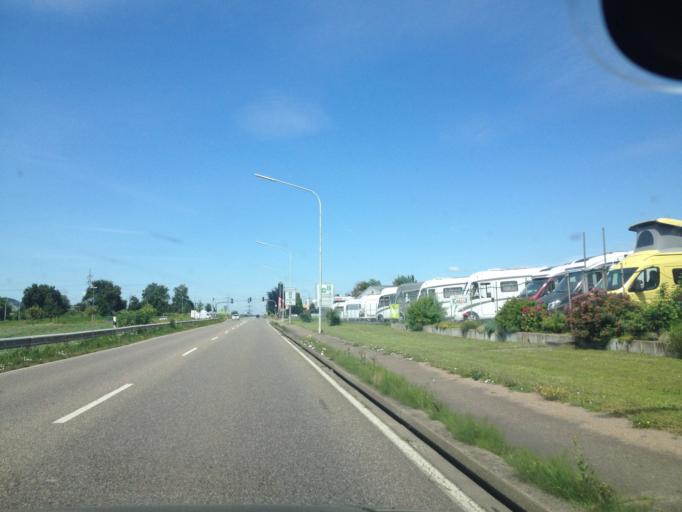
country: DE
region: Baden-Wuerttemberg
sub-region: Regierungsbezirk Stuttgart
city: Nordheim
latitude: 49.1400
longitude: 9.1670
